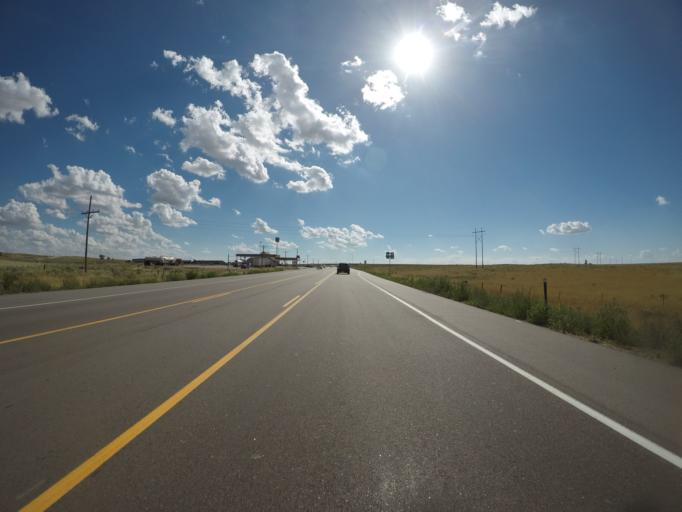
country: US
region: Colorado
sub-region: Logan County
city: Sterling
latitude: 40.6232
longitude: -103.1660
